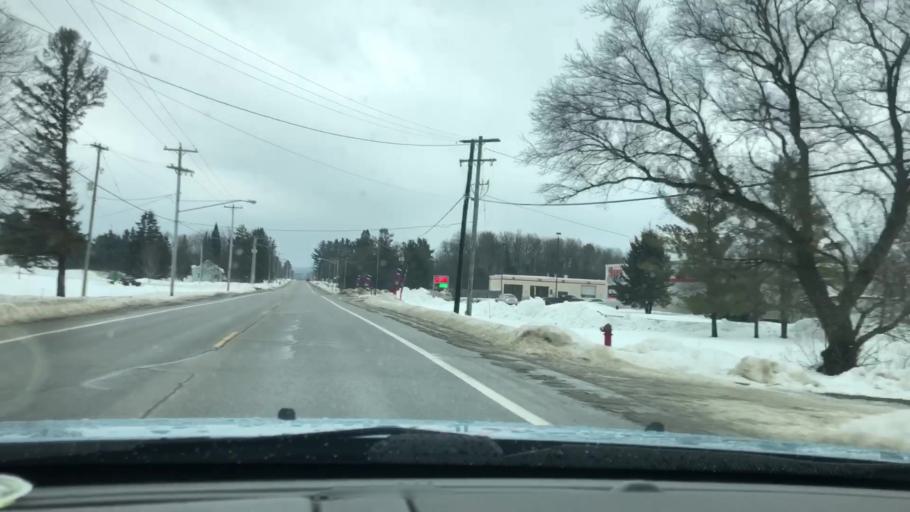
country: US
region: Michigan
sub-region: Charlevoix County
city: East Jordan
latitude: 45.1494
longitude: -85.1192
